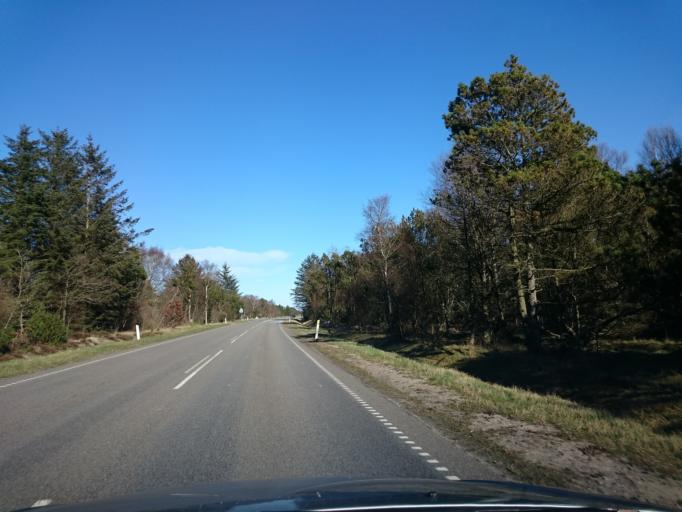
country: DK
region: North Denmark
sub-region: Frederikshavn Kommune
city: Strandby
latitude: 57.6066
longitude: 10.3914
